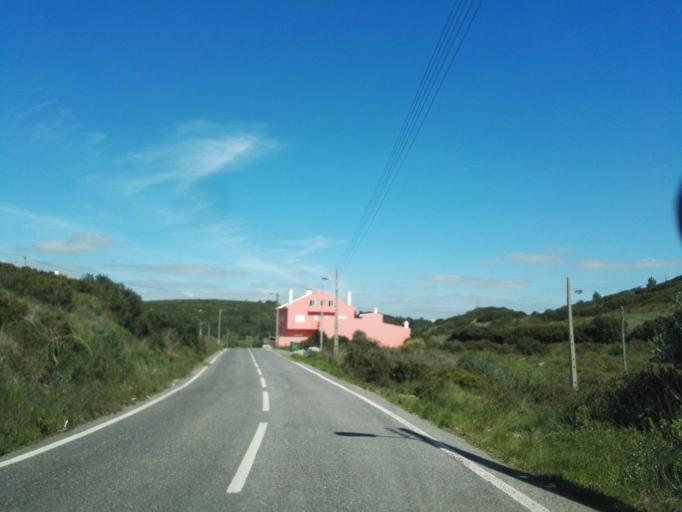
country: PT
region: Lisbon
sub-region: Sintra
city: Rio de Mouro
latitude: 38.7531
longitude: -9.3312
